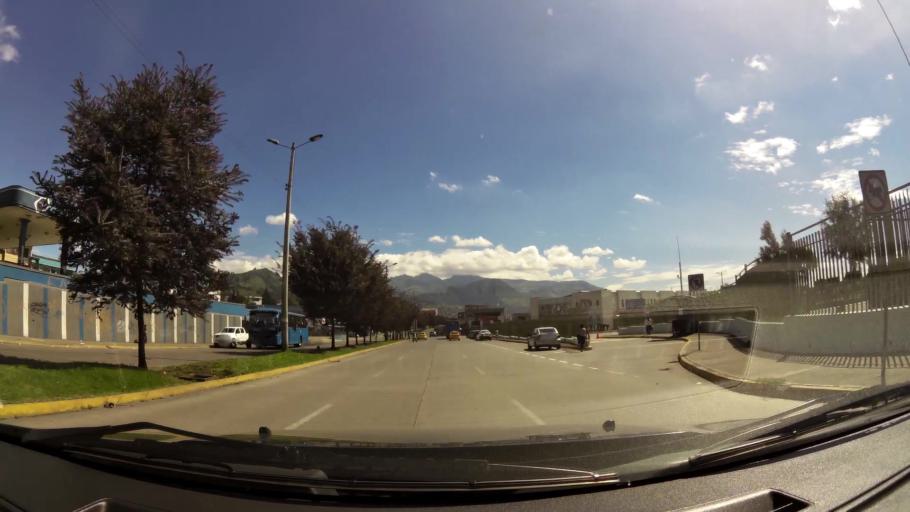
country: EC
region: Pichincha
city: Quito
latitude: -0.2979
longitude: -78.5586
